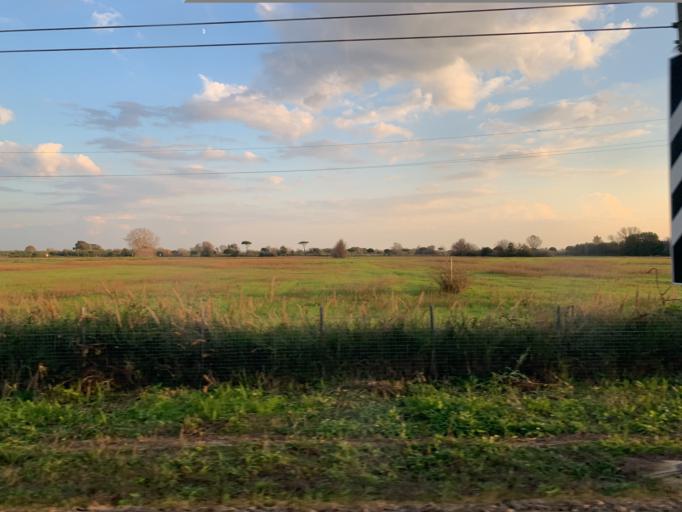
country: IT
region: Latium
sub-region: Citta metropolitana di Roma Capitale
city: Npp 23 (Parco Leonardo)
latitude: 41.7892
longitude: 12.2725
